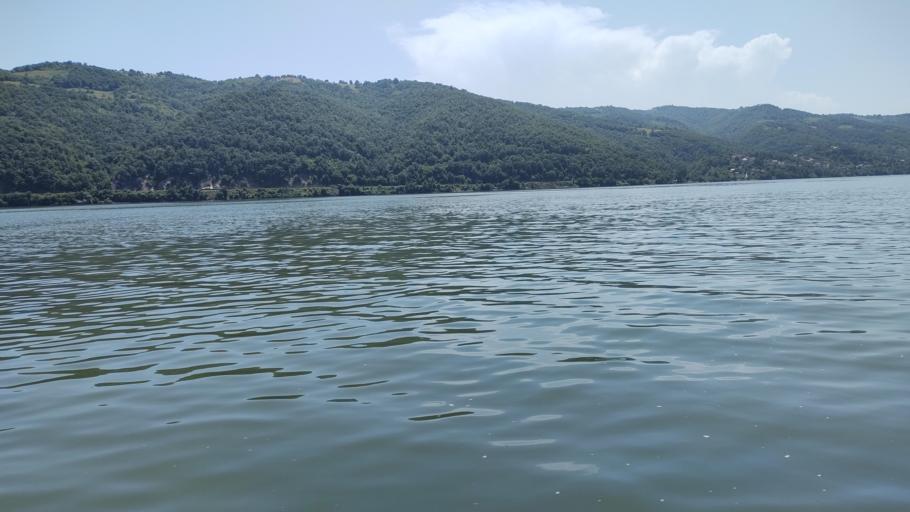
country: RO
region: Mehedinti
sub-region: Comuna Svinita
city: Svinita
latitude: 44.5156
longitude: 22.1989
